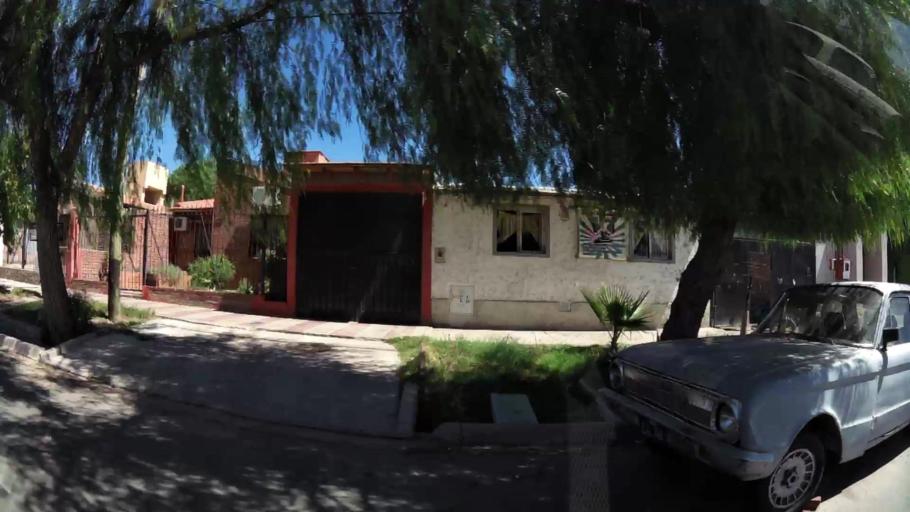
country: AR
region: Mendoza
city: Las Heras
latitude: -32.8372
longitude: -68.8724
